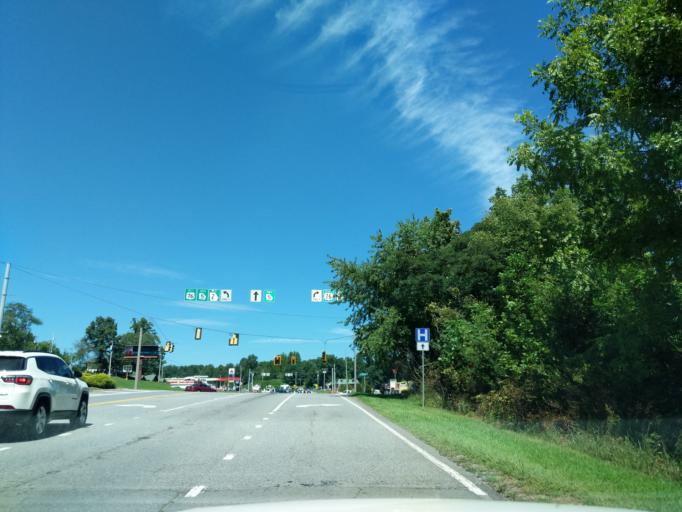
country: US
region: Georgia
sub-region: Fannin County
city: Blue Ridge
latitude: 34.8721
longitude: -84.3231
